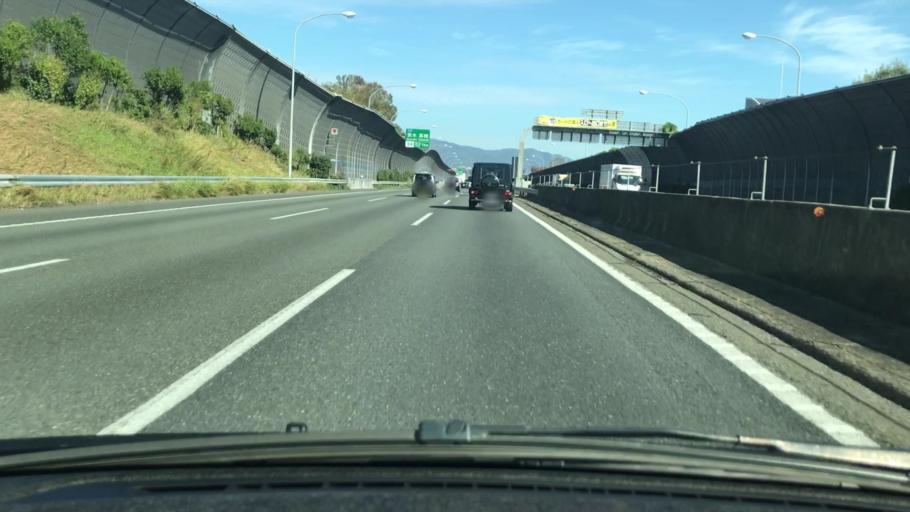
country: JP
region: Osaka
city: Ibaraki
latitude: 34.8211
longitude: 135.5527
